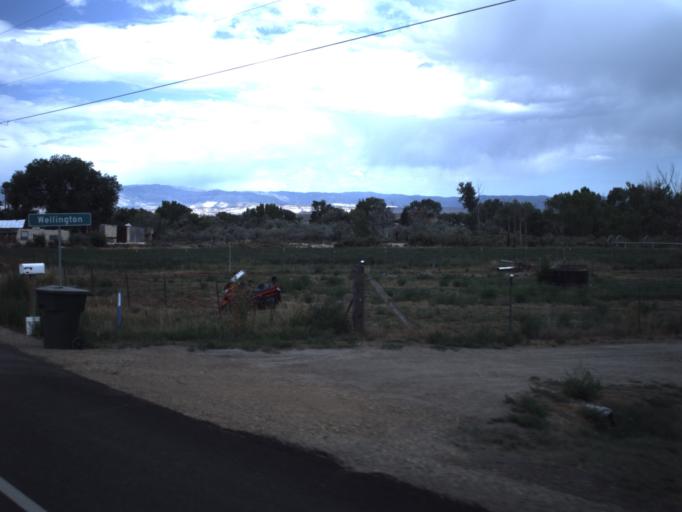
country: US
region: Utah
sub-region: Carbon County
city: Wellington
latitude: 39.5438
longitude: -110.6817
